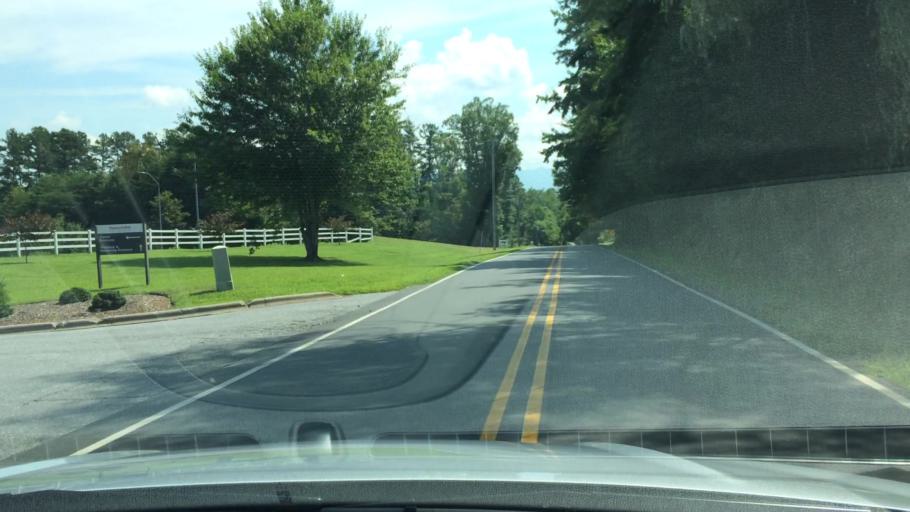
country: US
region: North Carolina
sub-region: Buncombe County
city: Weaverville
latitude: 35.6842
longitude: -82.5794
